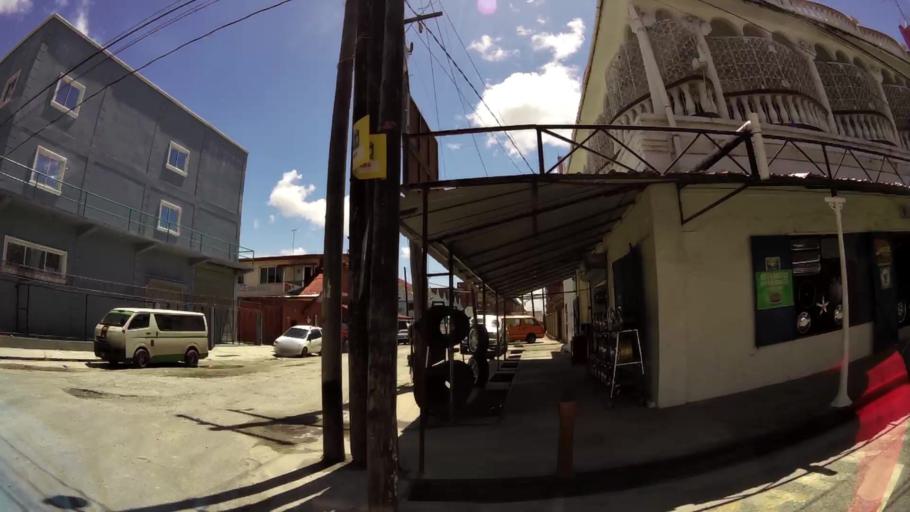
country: GY
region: Demerara-Mahaica
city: Georgetown
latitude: 6.8071
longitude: -58.1675
